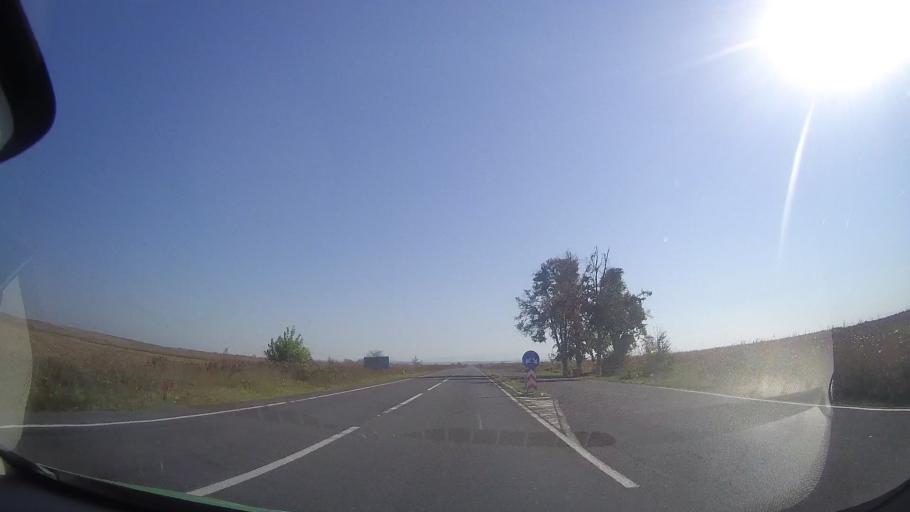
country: RO
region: Timis
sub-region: Comuna Belint
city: Belint
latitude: 45.7462
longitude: 21.7954
